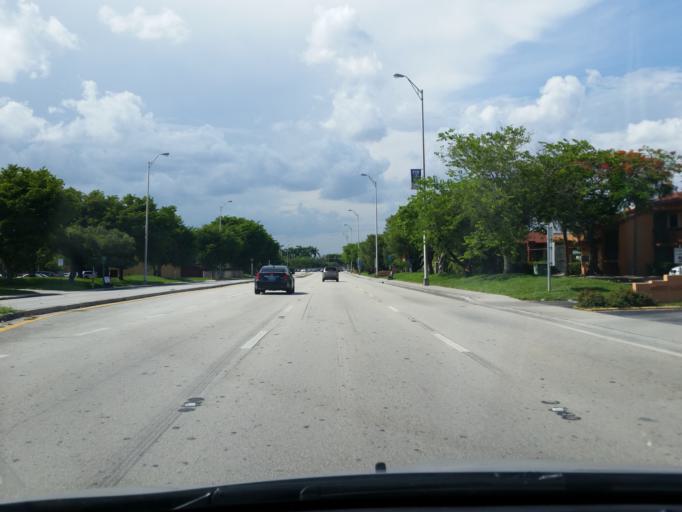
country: US
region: Florida
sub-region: Miami-Dade County
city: Sweetwater
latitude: 25.7726
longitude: -80.3693
